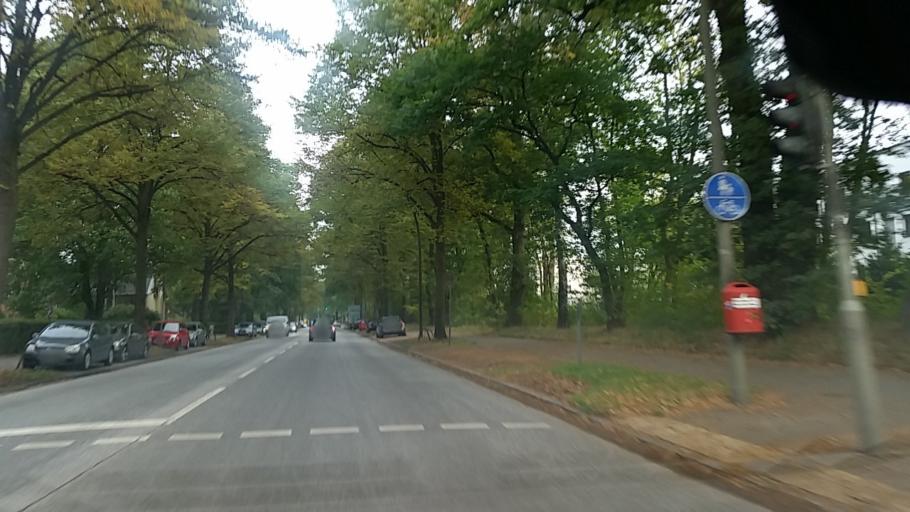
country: DE
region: Hamburg
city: Langenhorn
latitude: 53.6688
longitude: 10.0021
